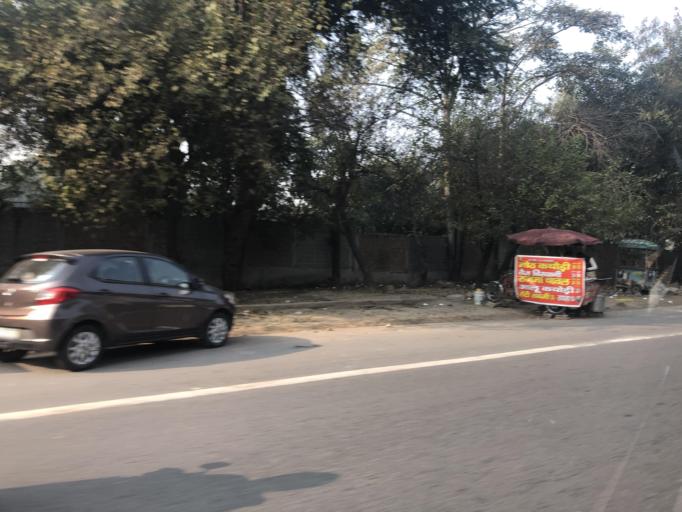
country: IN
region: NCT
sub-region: Central Delhi
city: Karol Bagh
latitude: 28.6009
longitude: 77.1603
